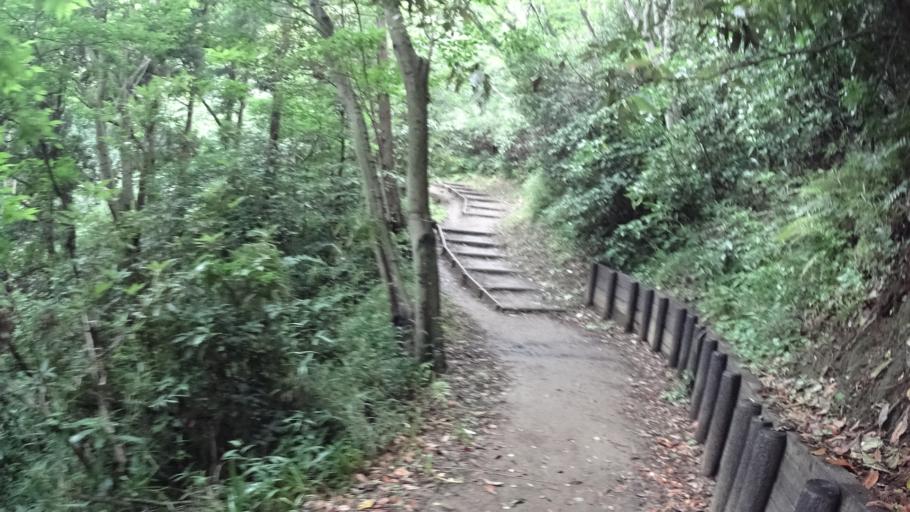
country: JP
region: Kanagawa
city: Zushi
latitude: 35.3572
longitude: 139.6089
